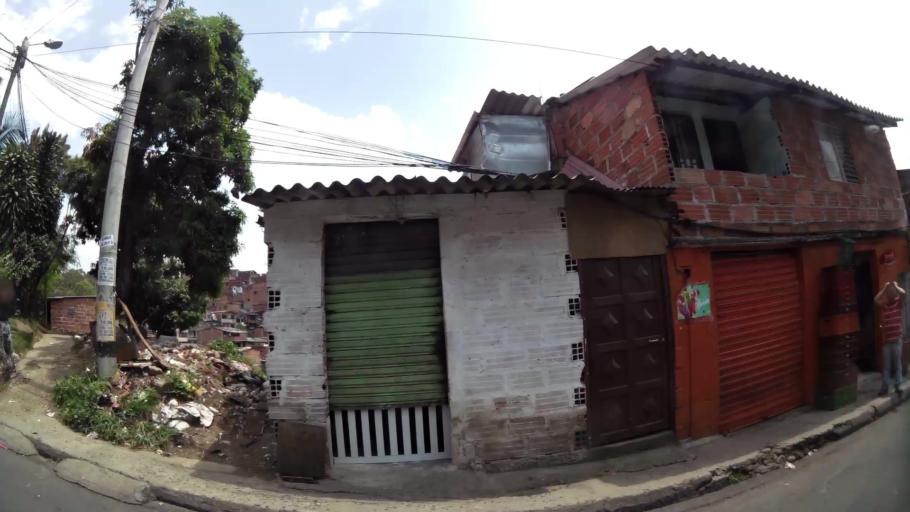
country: CO
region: Antioquia
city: Itagui
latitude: 6.1784
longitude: -75.6124
